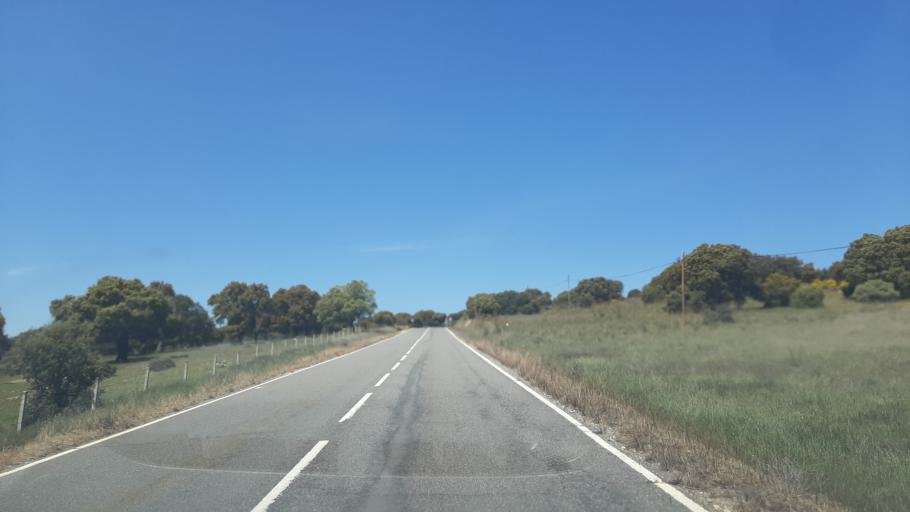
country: ES
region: Castille and Leon
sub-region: Provincia de Salamanca
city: Puente del Congosto
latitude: 40.5286
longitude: -5.5167
